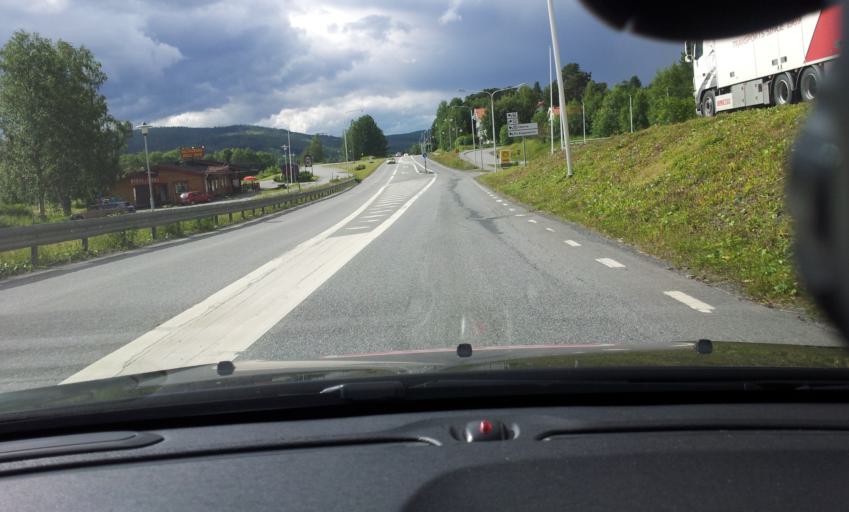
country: SE
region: Jaemtland
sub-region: Are Kommun
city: Jarpen
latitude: 63.3424
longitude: 13.4740
